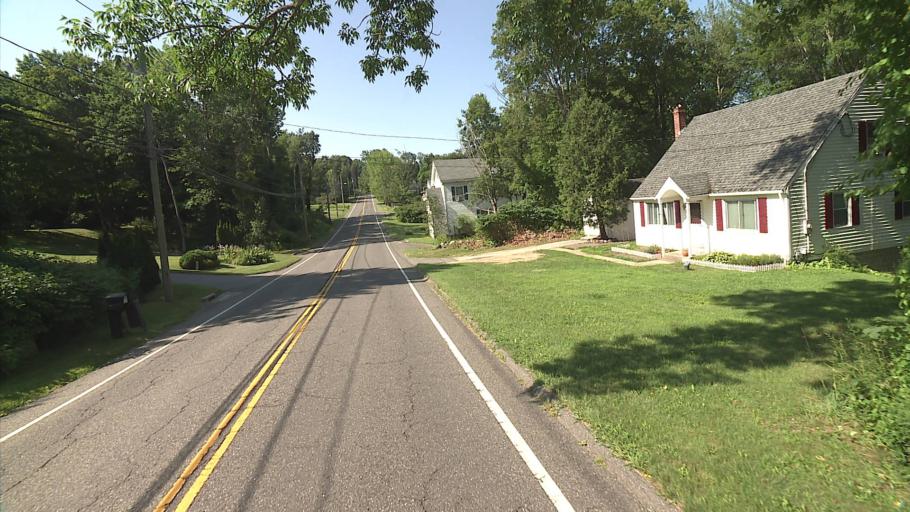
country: US
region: Connecticut
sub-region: Litchfield County
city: Winsted
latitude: 41.9058
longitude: -73.0598
